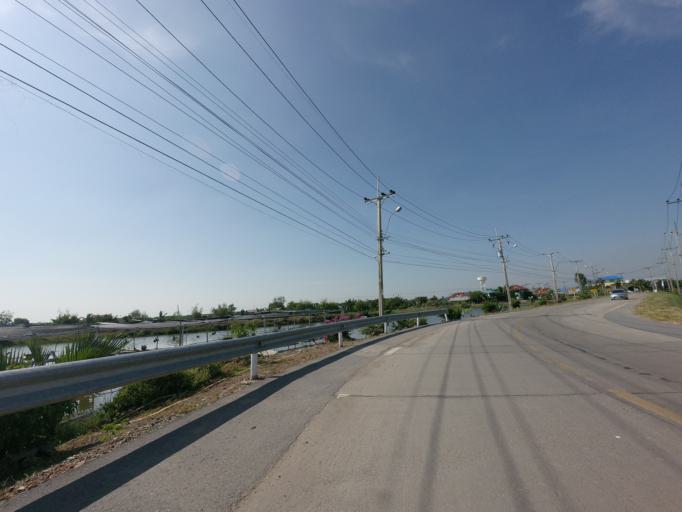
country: TH
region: Samut Prakan
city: Phra Samut Chedi
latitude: 13.5522
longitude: 100.5369
